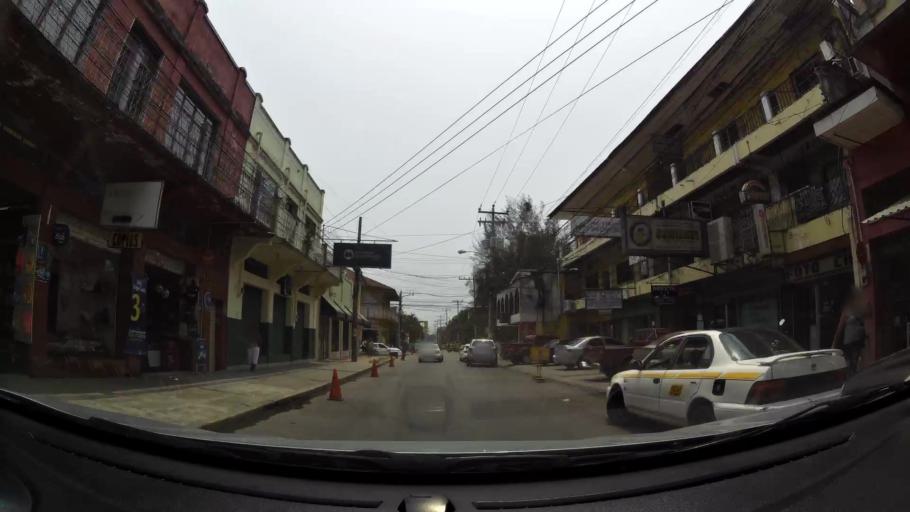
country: HN
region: Yoro
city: El Progreso
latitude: 15.4008
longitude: -87.8112
